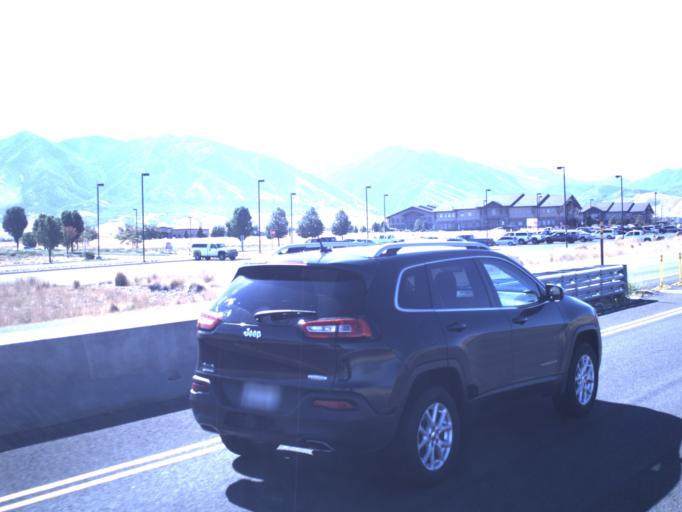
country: US
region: Utah
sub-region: Tooele County
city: Erda
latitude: 40.5756
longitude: -112.2947
